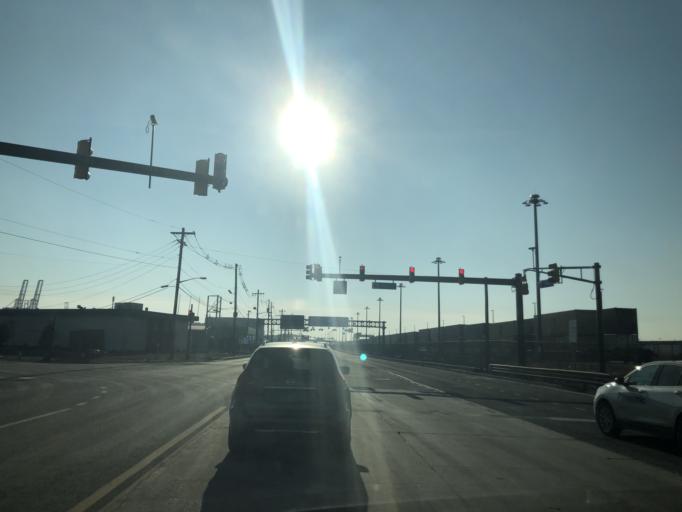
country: US
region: New Jersey
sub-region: Essex County
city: Newark
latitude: 40.6970
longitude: -74.1550
